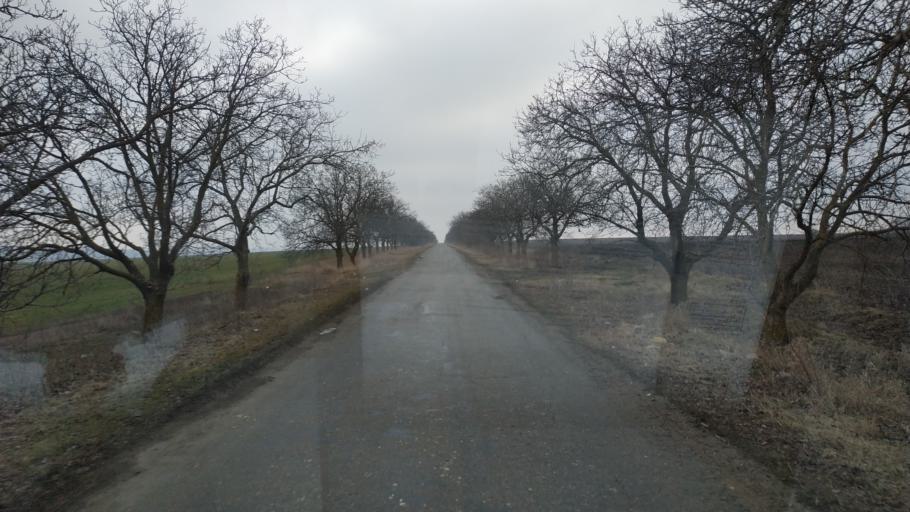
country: MD
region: Hincesti
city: Dancu
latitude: 46.8976
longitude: 28.3041
